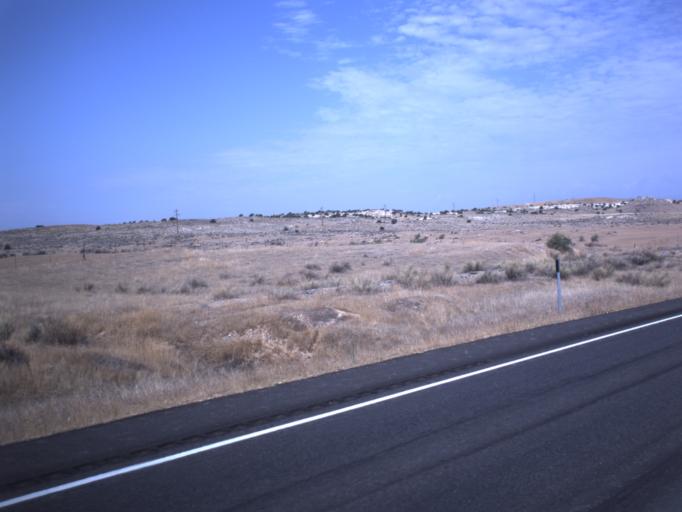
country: US
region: Utah
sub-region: Uintah County
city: Naples
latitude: 40.3436
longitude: -109.2999
